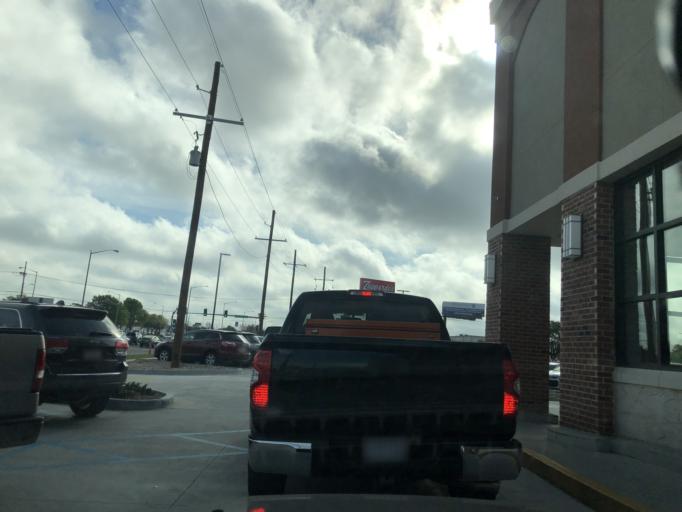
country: US
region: Louisiana
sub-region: Jefferson Parish
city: Metairie Terrace
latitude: 30.0054
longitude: -90.1961
